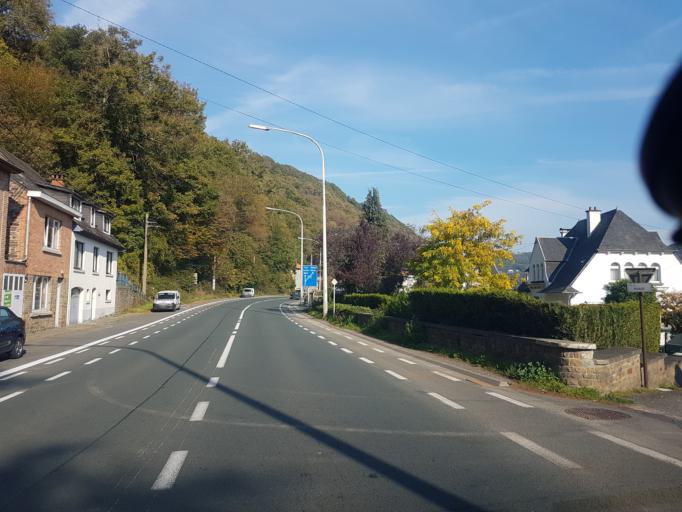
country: BE
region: Wallonia
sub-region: Province de Namur
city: Profondeville
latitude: 50.3624
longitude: 4.8705
